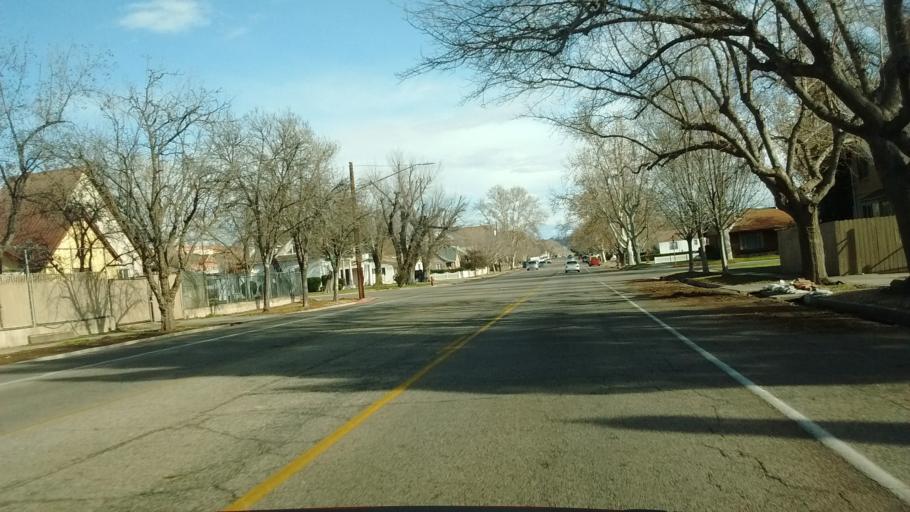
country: US
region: Utah
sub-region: Washington County
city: Saint George
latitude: 37.1065
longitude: -113.5883
